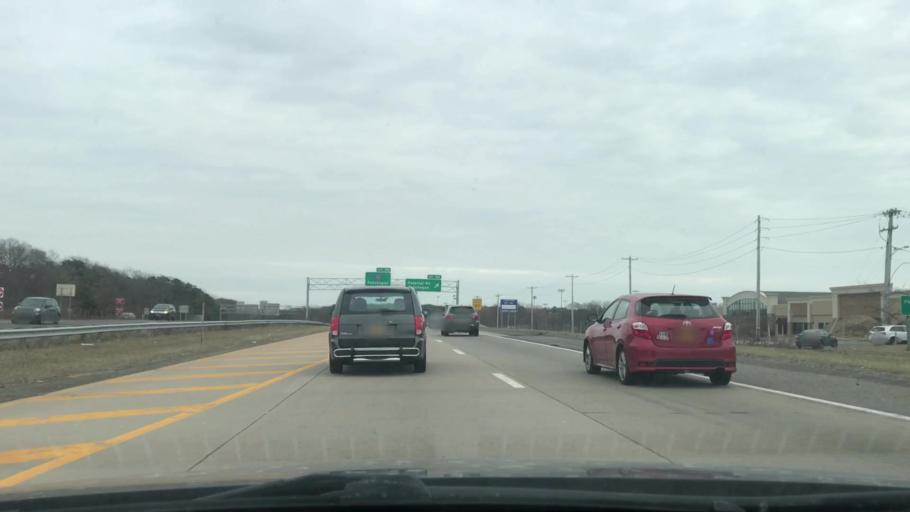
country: US
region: New York
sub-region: Suffolk County
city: North Patchogue
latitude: 40.7802
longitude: -72.9980
